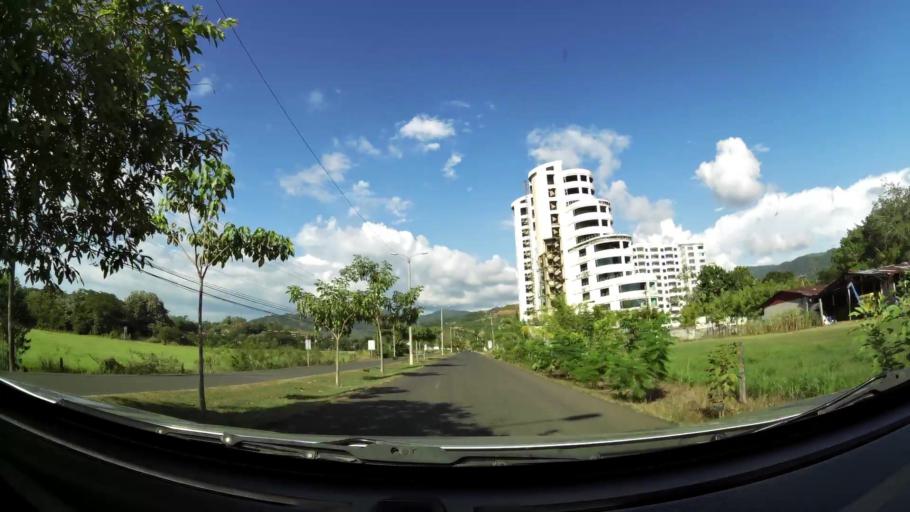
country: CR
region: Puntarenas
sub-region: Canton de Garabito
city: Jaco
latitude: 9.6320
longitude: -84.6300
